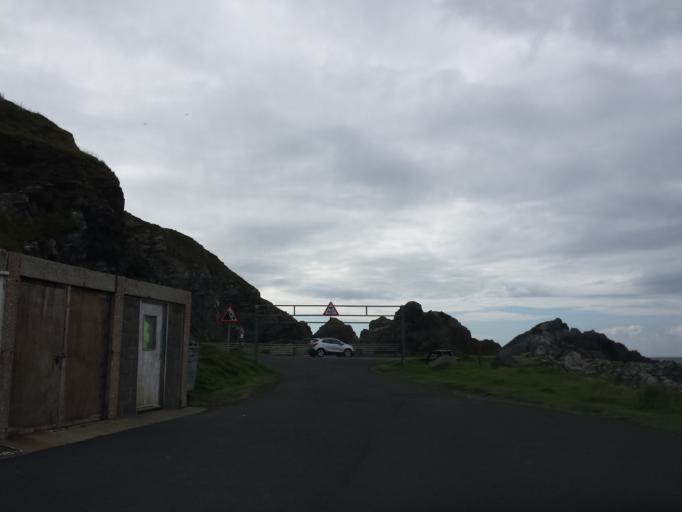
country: GB
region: Scotland
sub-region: Dumfries and Galloway
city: Stranraer
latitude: 54.8390
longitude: -5.1160
